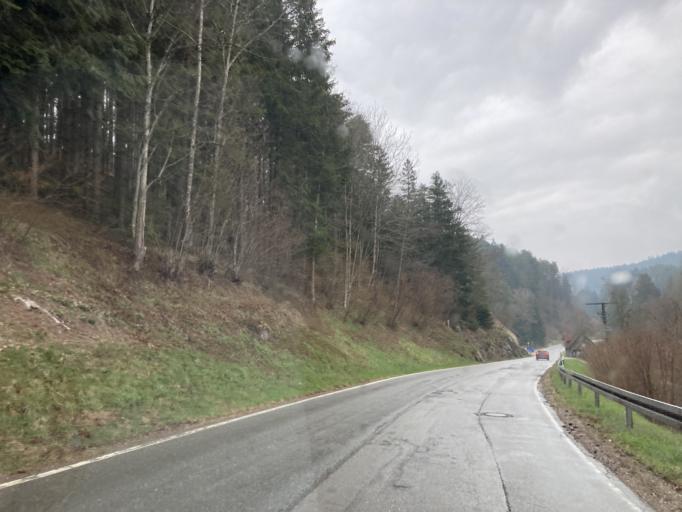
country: DE
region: Baden-Wuerttemberg
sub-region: Freiburg Region
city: Lauterbach/Schwarzwald
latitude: 48.2288
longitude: 8.3163
